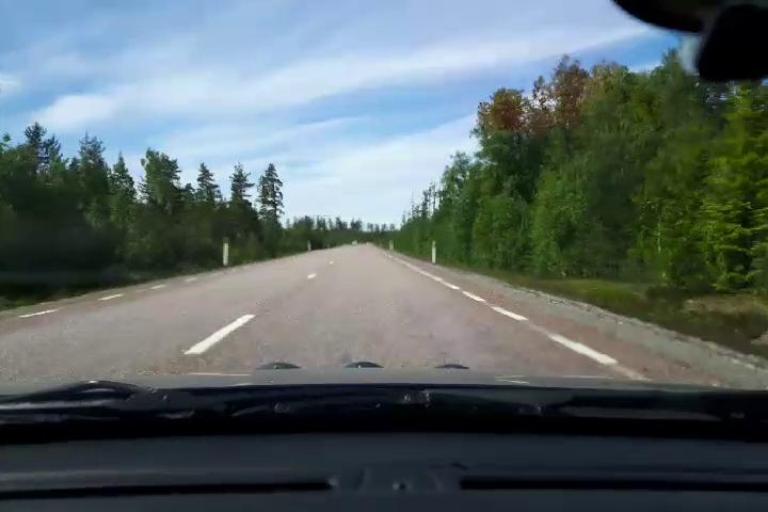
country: SE
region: Gaevleborg
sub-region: Soderhamns Kommun
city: Ljusne
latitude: 61.0855
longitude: 16.9583
